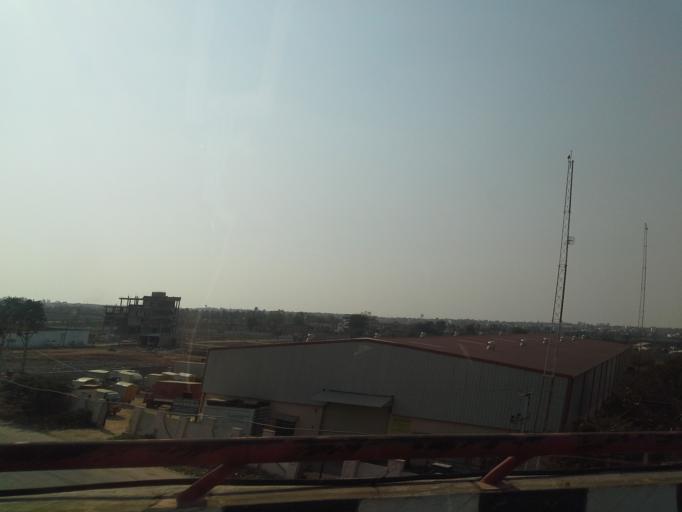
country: IN
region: Telangana
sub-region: Rangareddi
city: Sriramnagar
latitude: 17.2553
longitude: 78.3814
